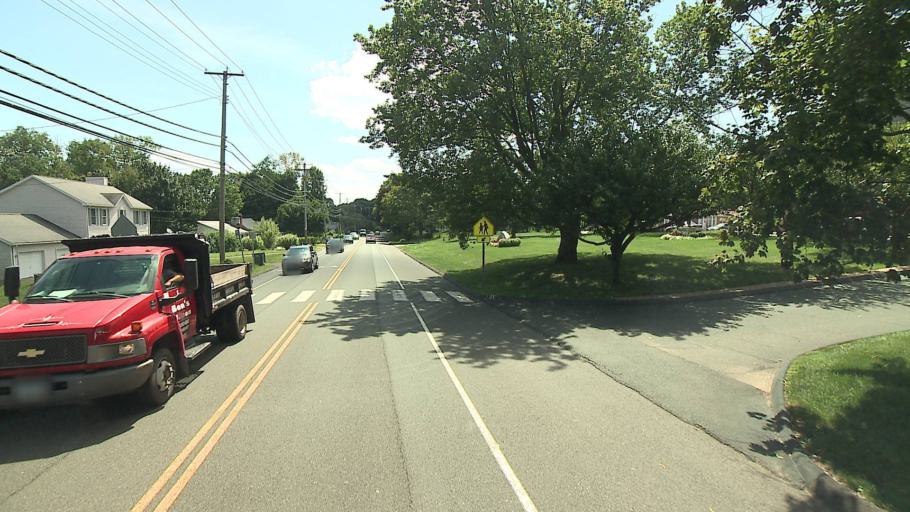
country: US
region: Connecticut
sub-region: Fairfield County
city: Trumbull
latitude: 41.2383
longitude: -73.2204
